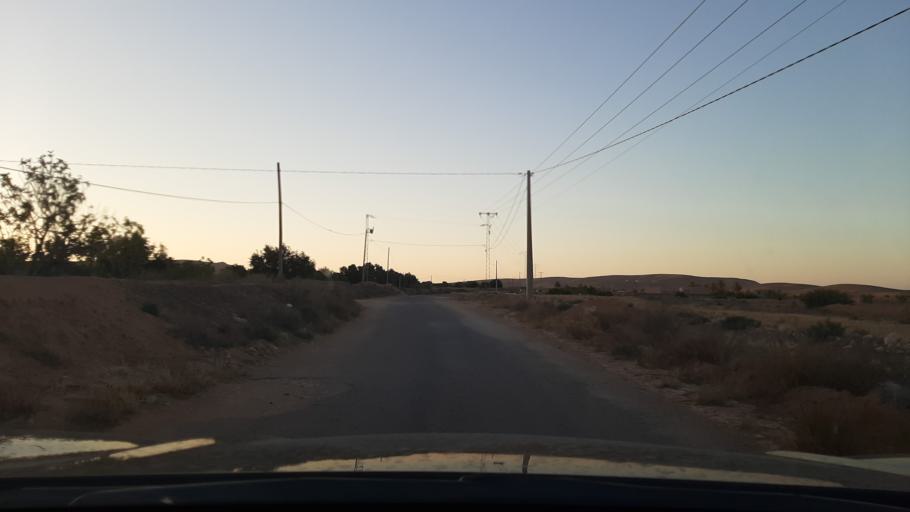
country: TN
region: Qabis
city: Matmata
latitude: 33.5531
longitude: 10.1866
